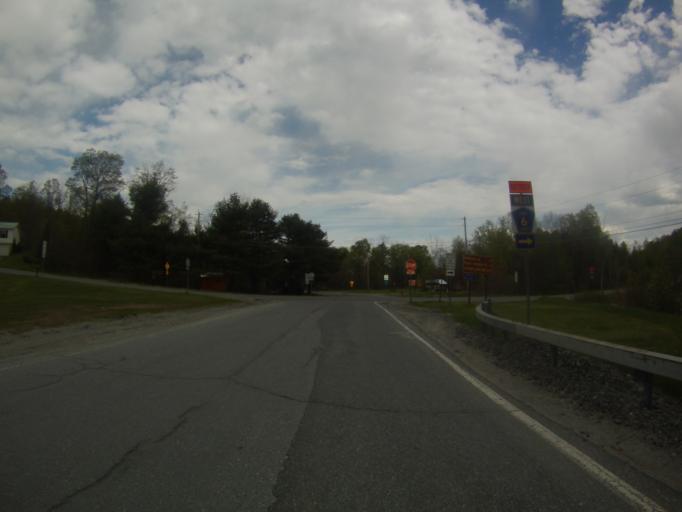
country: US
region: New York
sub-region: Essex County
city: Mineville
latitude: 44.0900
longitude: -73.5378
